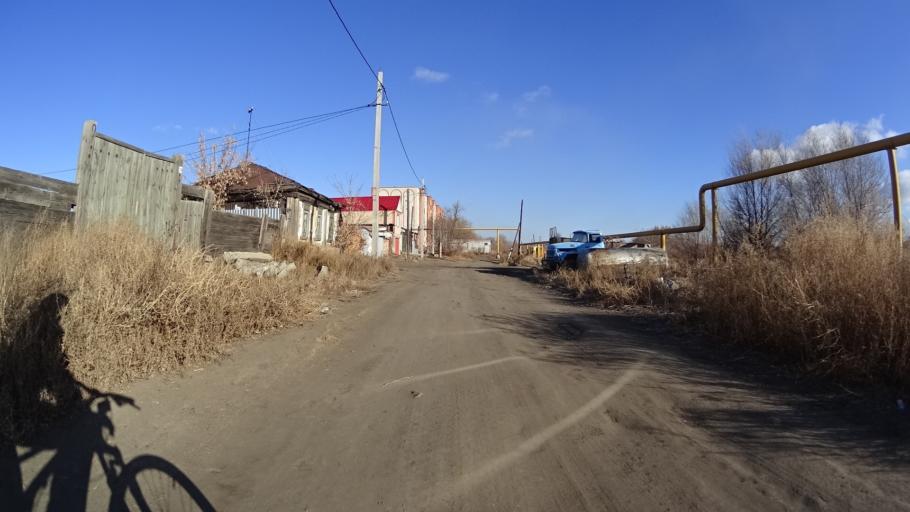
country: RU
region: Chelyabinsk
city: Troitsk
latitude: 54.0831
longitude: 61.5723
